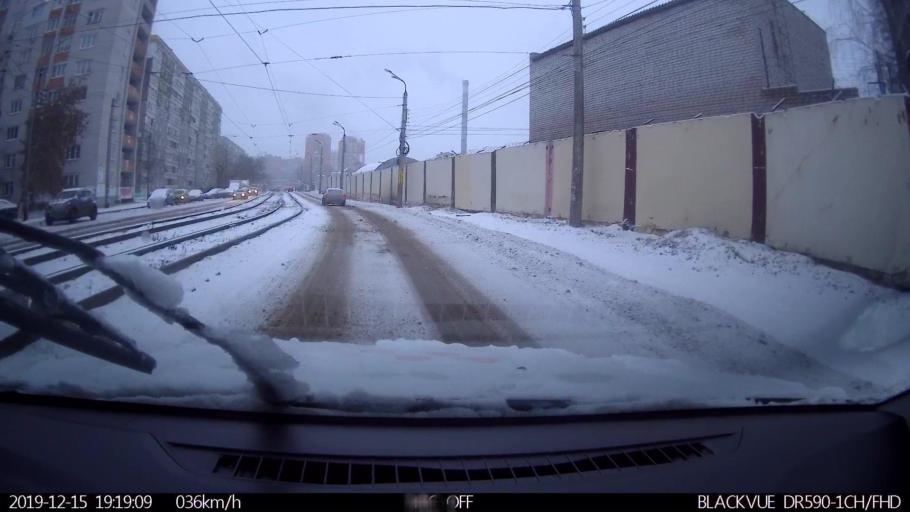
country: RU
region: Nizjnij Novgorod
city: Neklyudovo
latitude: 56.3525
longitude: 43.8558
